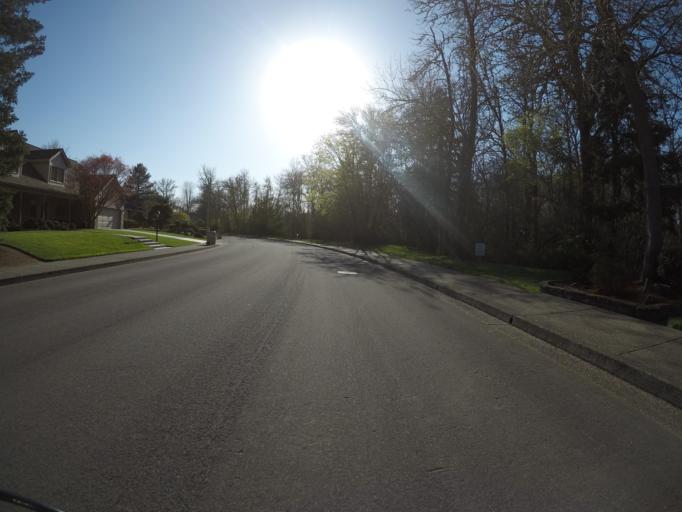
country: US
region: Oregon
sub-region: Washington County
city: Cedar Mill
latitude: 45.5434
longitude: -122.8138
